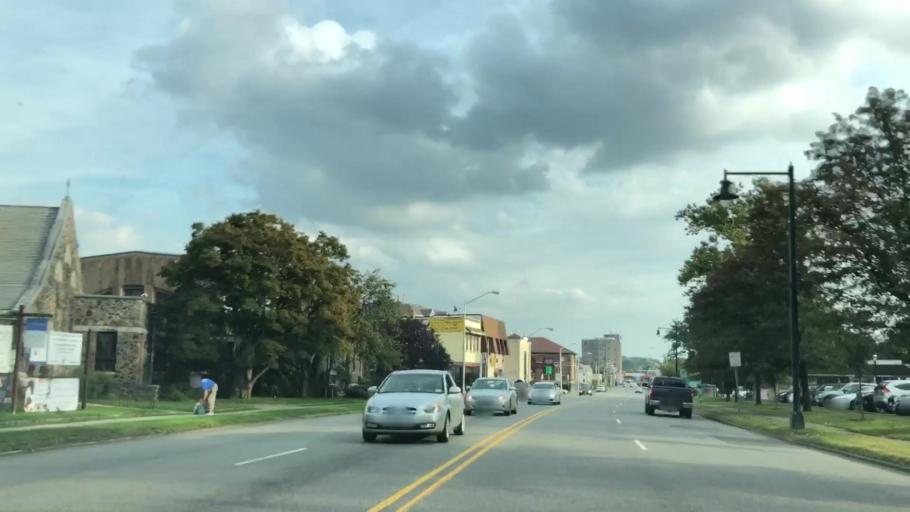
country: US
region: New Jersey
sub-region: Essex County
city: Glen Ridge
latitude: 40.7989
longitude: -74.2017
